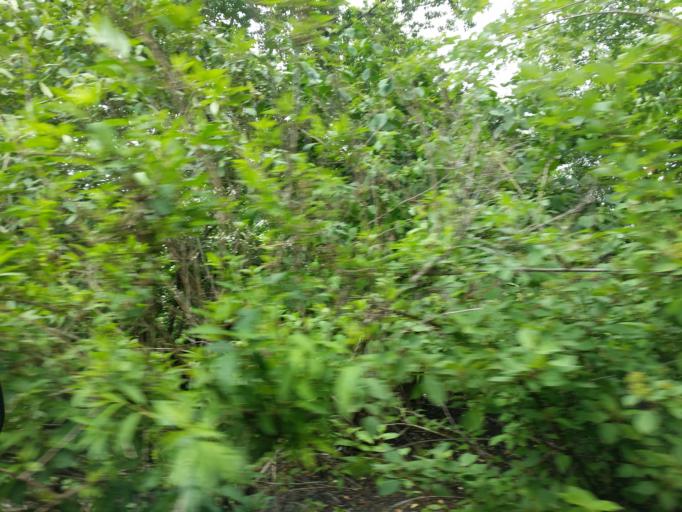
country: US
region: New York
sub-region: Nassau County
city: Hewlett
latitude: 40.6351
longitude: -73.6946
